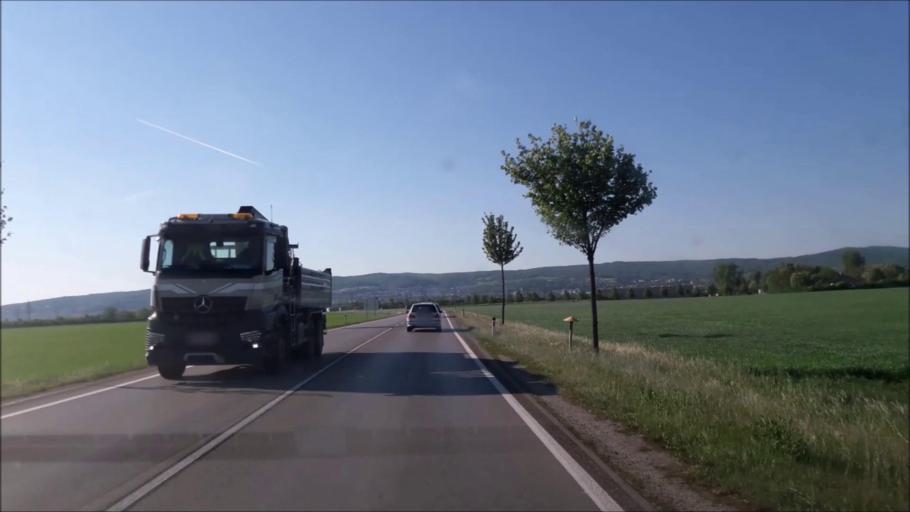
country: AT
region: Burgenland
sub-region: Eisenstadt-Umgebung
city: Trausdorf an der Wulka
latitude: 47.8166
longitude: 16.5465
